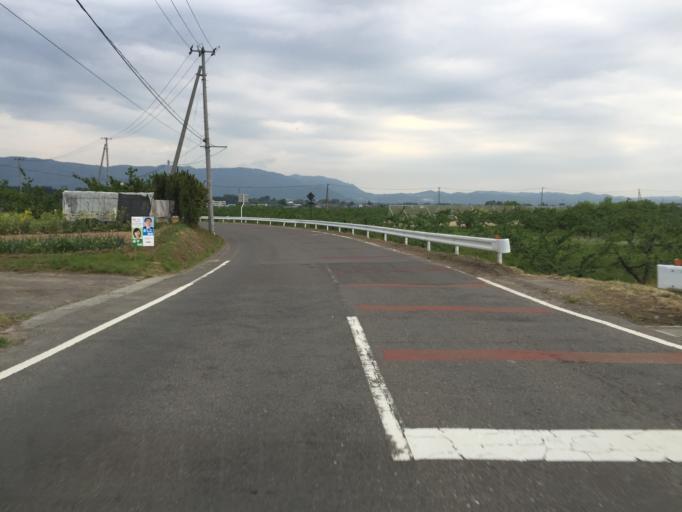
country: JP
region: Fukushima
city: Hobaramachi
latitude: 37.8398
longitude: 140.5381
